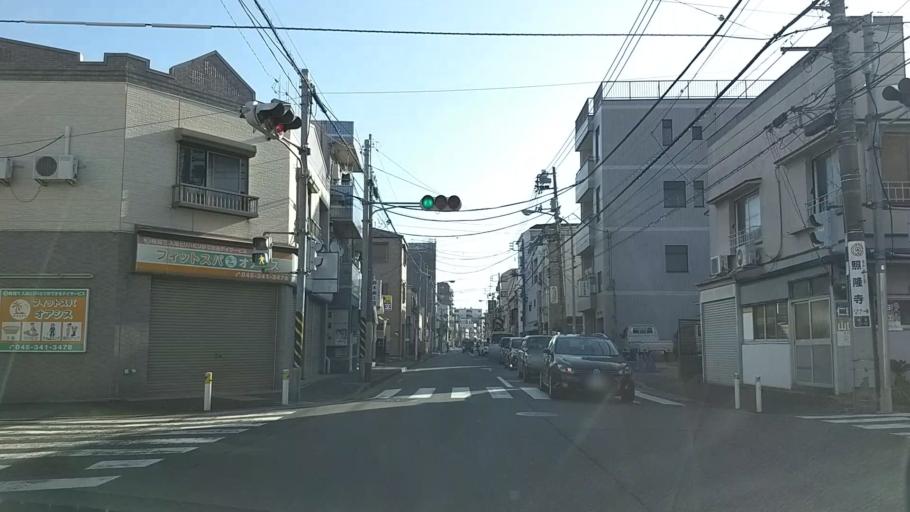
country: JP
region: Kanagawa
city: Yokohama
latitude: 35.4298
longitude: 139.6133
